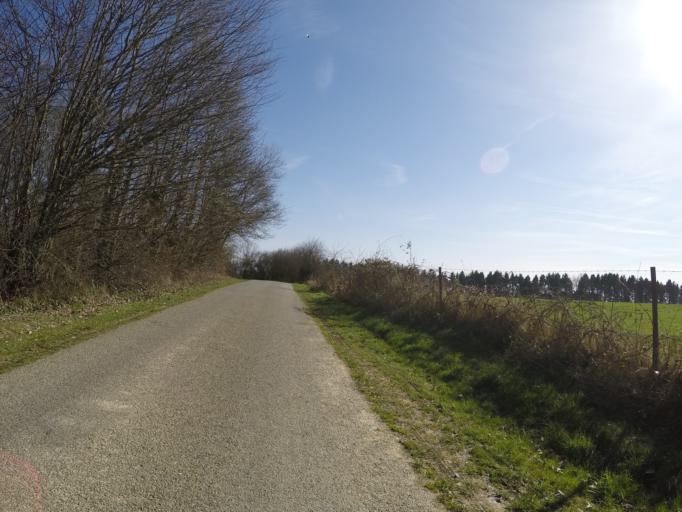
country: BE
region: Wallonia
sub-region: Province de Namur
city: Hamois
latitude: 50.3538
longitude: 5.1041
